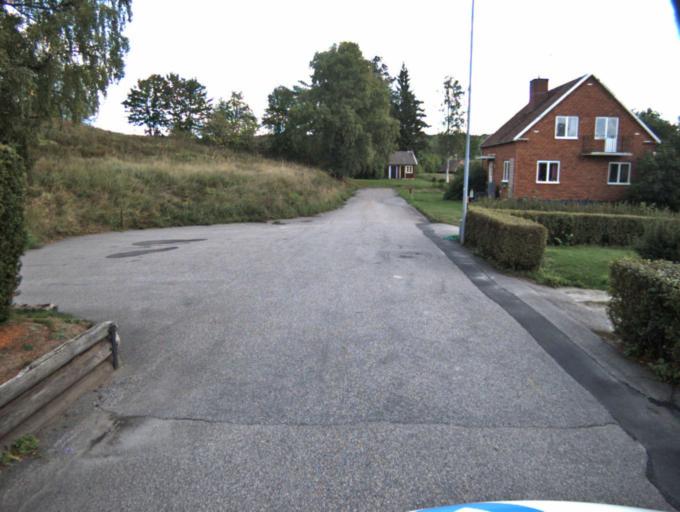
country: SE
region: Vaestra Goetaland
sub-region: Ulricehamns Kommun
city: Ulricehamn
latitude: 57.9312
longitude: 13.4980
